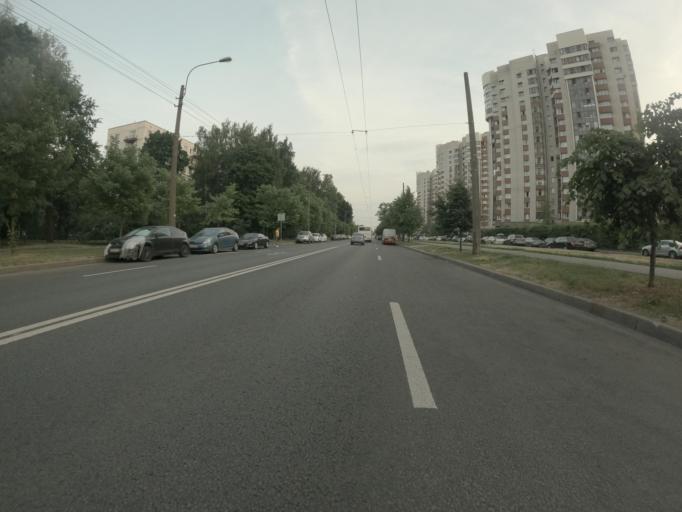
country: RU
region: Leningrad
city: Kalininskiy
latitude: 59.9822
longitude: 30.3972
